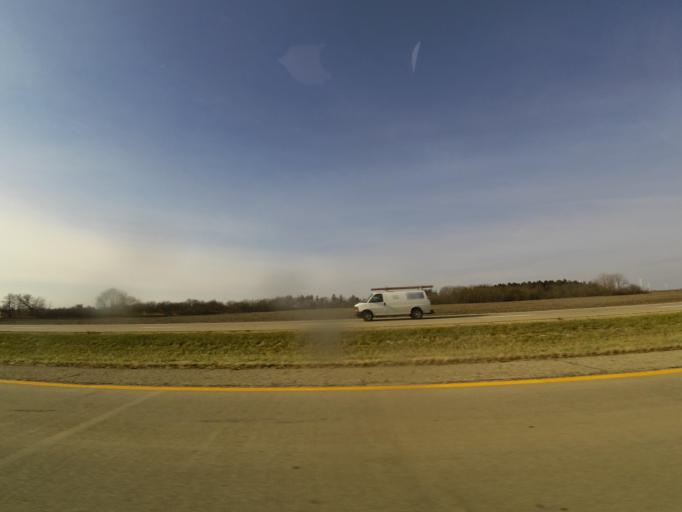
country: US
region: Illinois
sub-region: Macon County
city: Forsyth
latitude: 39.9617
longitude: -88.9559
